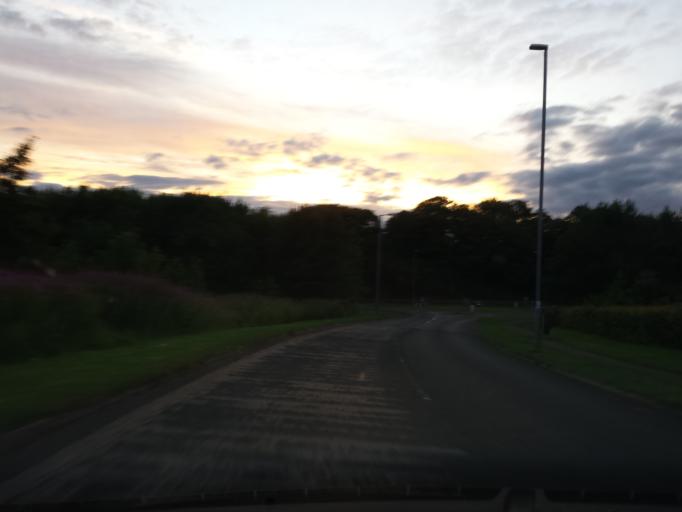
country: GB
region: Scotland
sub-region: The Scottish Borders
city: Eyemouth
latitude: 55.8617
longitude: -2.0883
